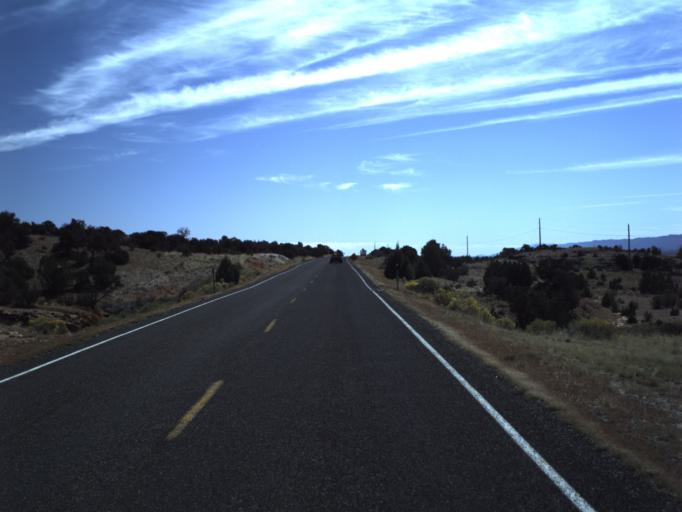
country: US
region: Utah
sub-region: Wayne County
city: Loa
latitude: 37.7338
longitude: -111.5411
